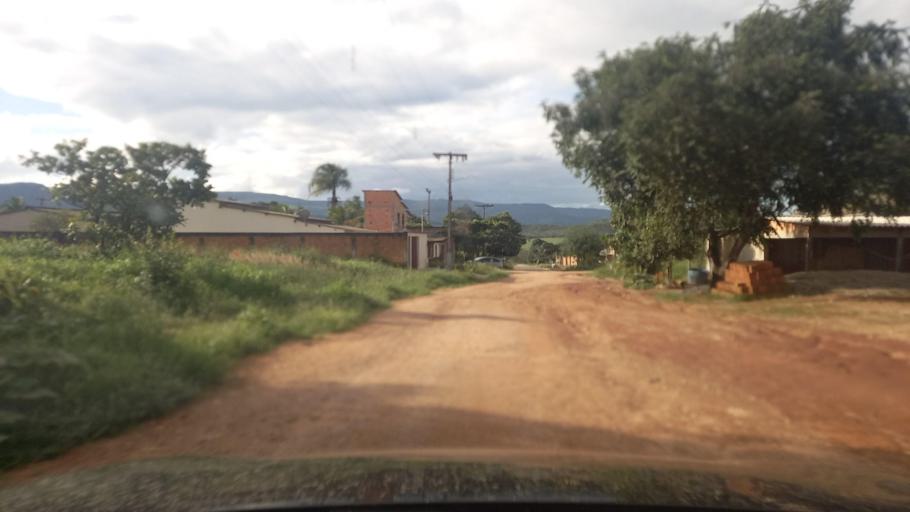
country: BR
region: Goias
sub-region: Cavalcante
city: Cavalcante
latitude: -13.7974
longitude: -47.4439
